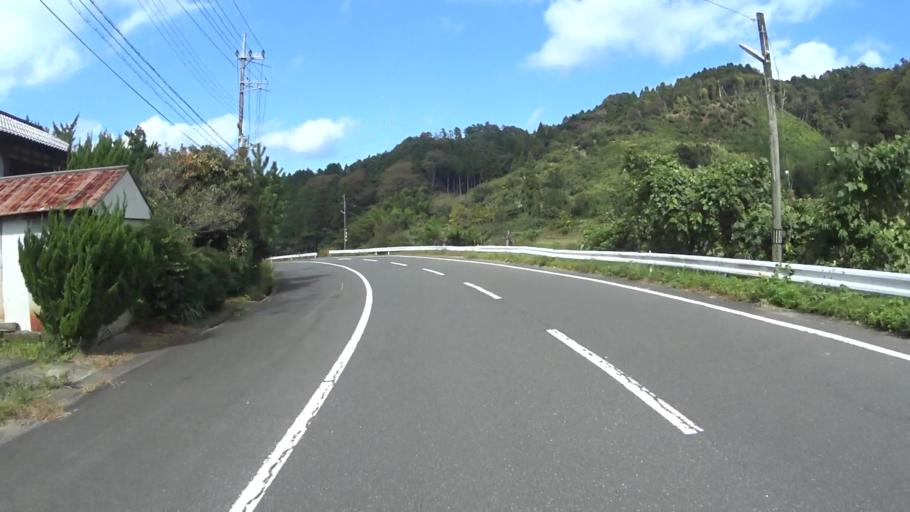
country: JP
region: Kyoto
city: Miyazu
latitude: 35.6897
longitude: 135.2530
